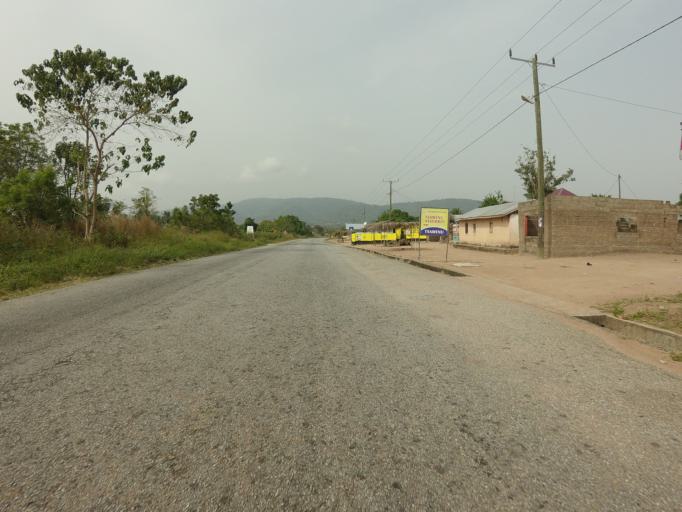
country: GH
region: Volta
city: Ho
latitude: 6.5758
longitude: 0.3327
